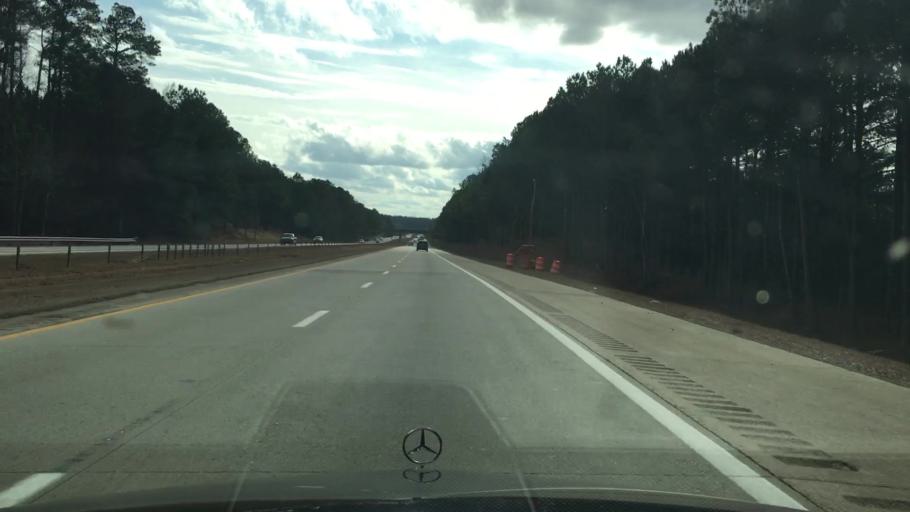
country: US
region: North Carolina
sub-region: Wake County
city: Garner
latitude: 35.5787
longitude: -78.5767
